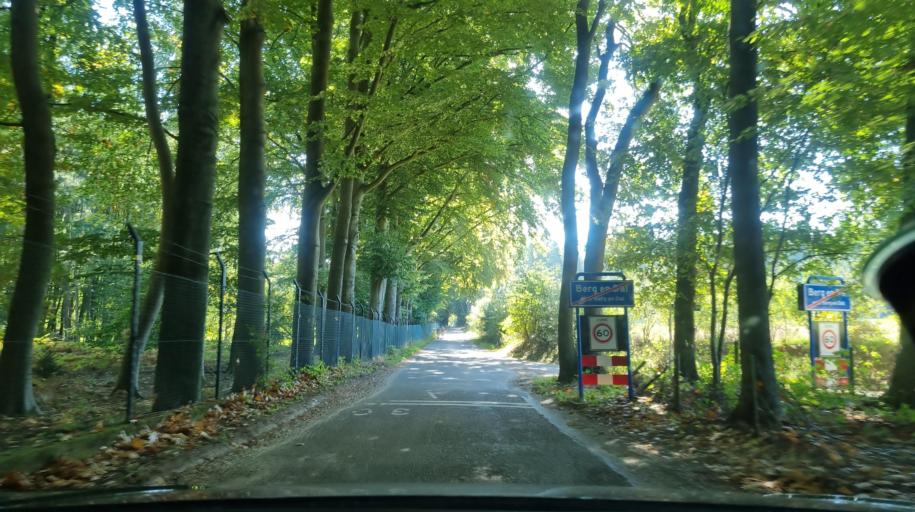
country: NL
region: Gelderland
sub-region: Gemeente Groesbeek
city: Berg en Dal
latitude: 51.8196
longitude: 5.9097
